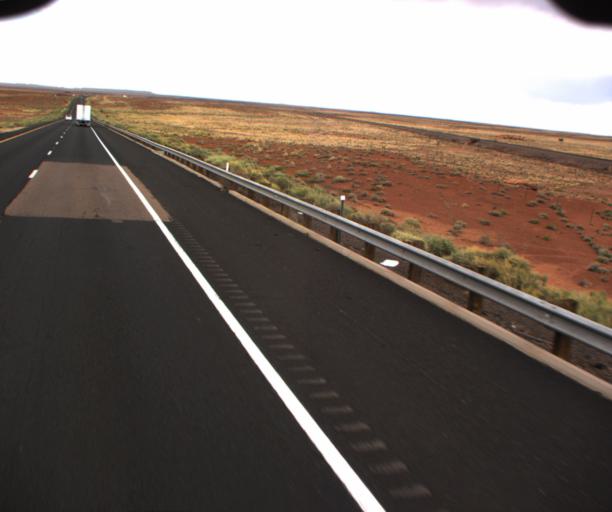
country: US
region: Arizona
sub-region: Coconino County
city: LeChee
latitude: 35.0991
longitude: -110.9710
